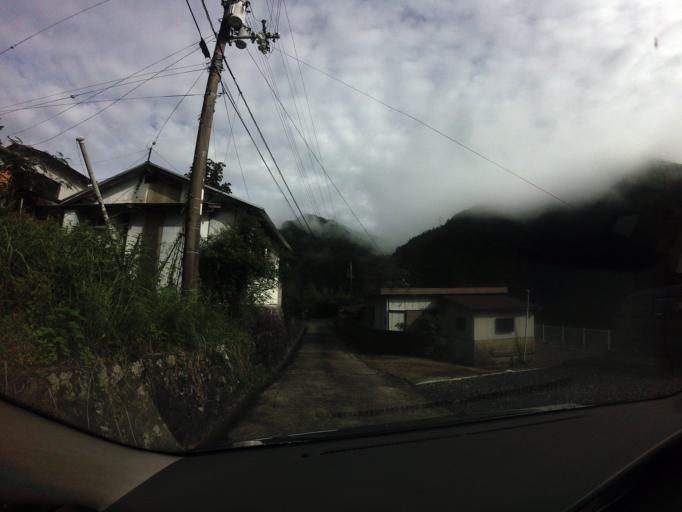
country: JP
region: Wakayama
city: Shingu
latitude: 33.9683
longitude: 135.8125
